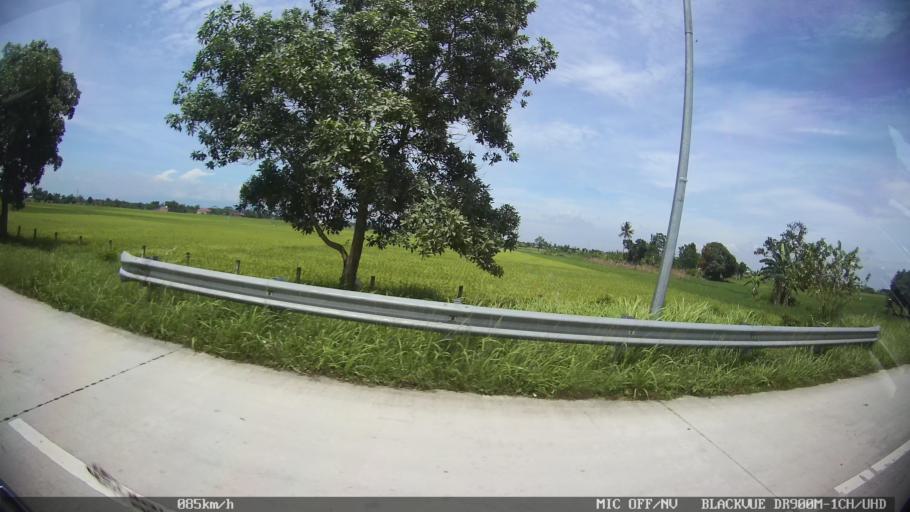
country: ID
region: North Sumatra
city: Perbaungan
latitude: 3.5447
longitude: 98.8906
